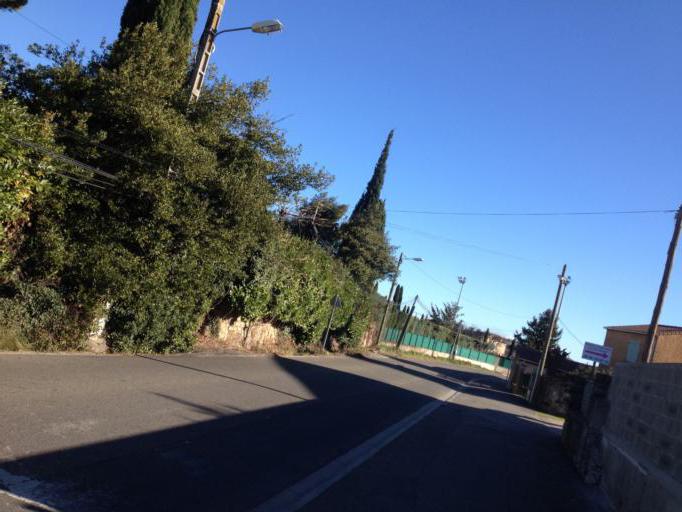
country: FR
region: Provence-Alpes-Cote d'Azur
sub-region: Departement du Vaucluse
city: Orange
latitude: 44.1481
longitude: 4.7992
